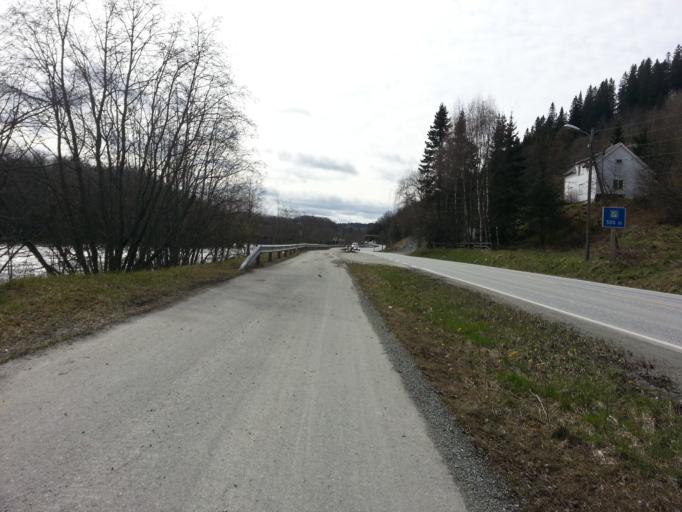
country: NO
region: Sor-Trondelag
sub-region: Trondheim
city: Trondheim
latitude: 63.3986
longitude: 10.3880
